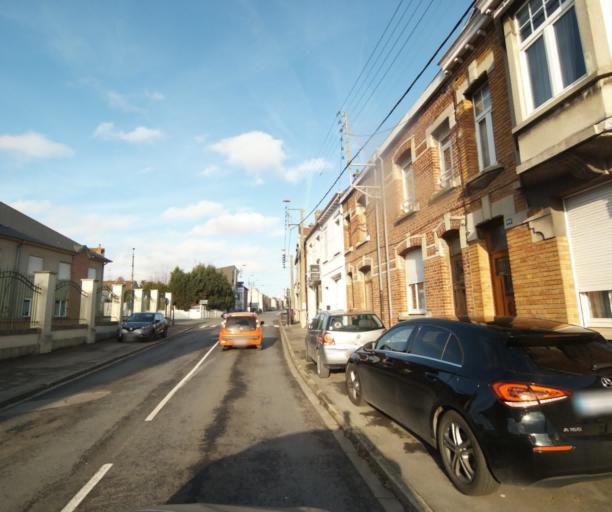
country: FR
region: Nord-Pas-de-Calais
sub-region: Departement du Nord
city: Valenciennes
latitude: 50.3616
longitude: 3.5412
